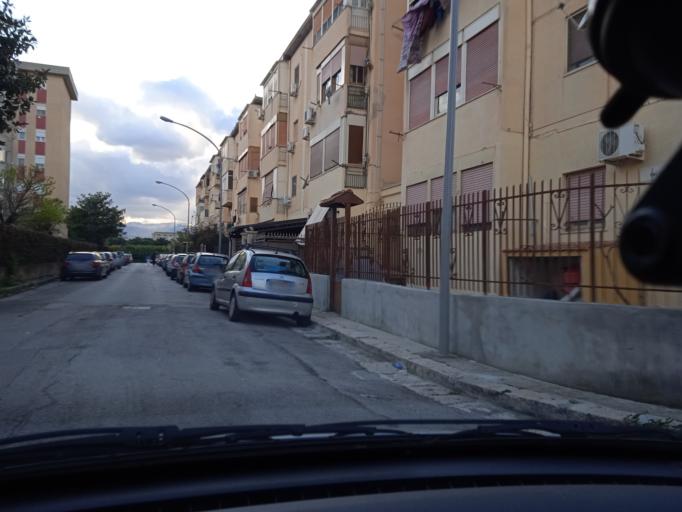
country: IT
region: Sicily
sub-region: Palermo
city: Villa Ciambra
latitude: 38.0838
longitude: 13.3578
